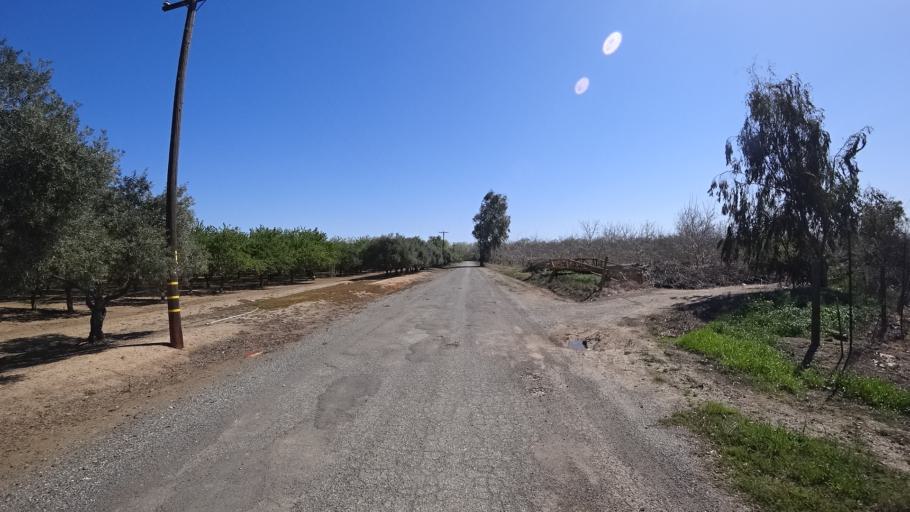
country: US
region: California
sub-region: Glenn County
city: Hamilton City
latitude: 39.7755
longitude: -122.0364
